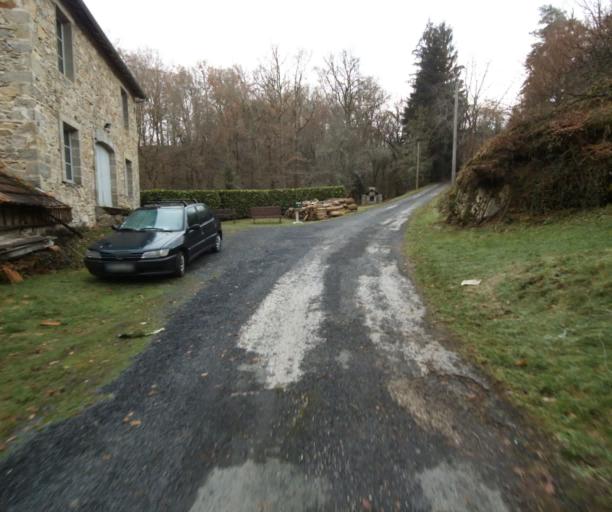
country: FR
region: Limousin
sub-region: Departement de la Correze
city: Chameyrat
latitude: 45.2281
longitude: 1.6905
